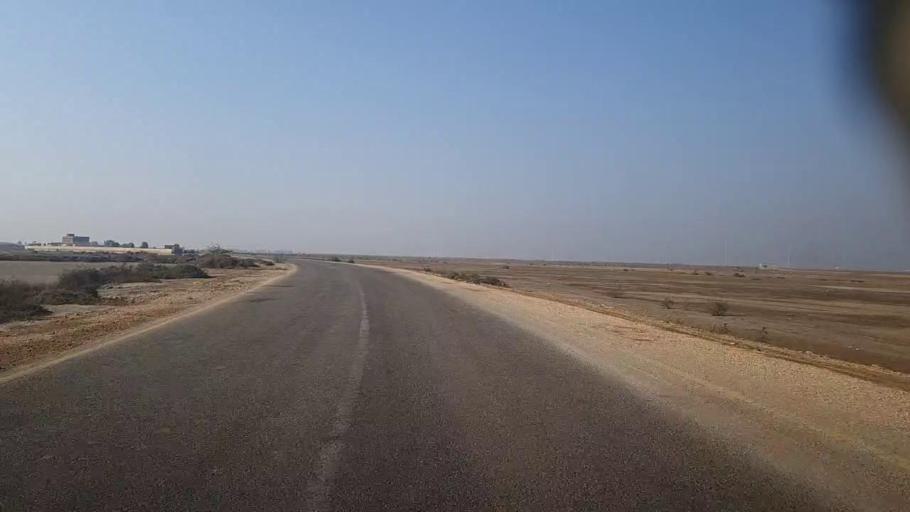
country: PK
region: Sindh
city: Gharo
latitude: 24.7029
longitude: 67.5292
